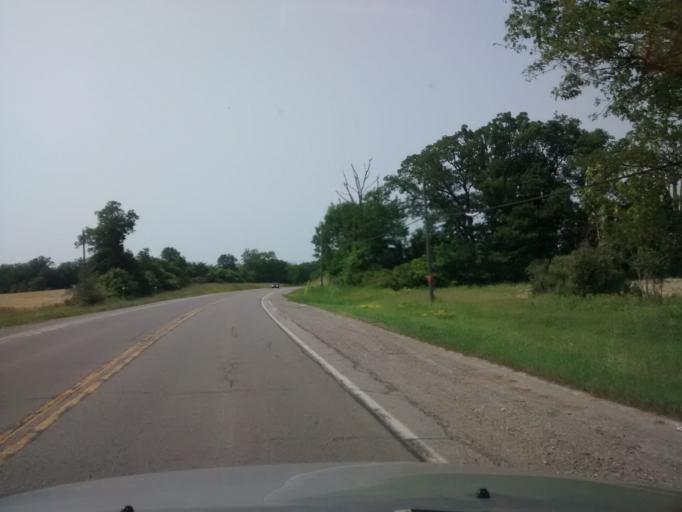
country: CA
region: Ontario
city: Ancaster
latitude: 42.9734
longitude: -79.8705
